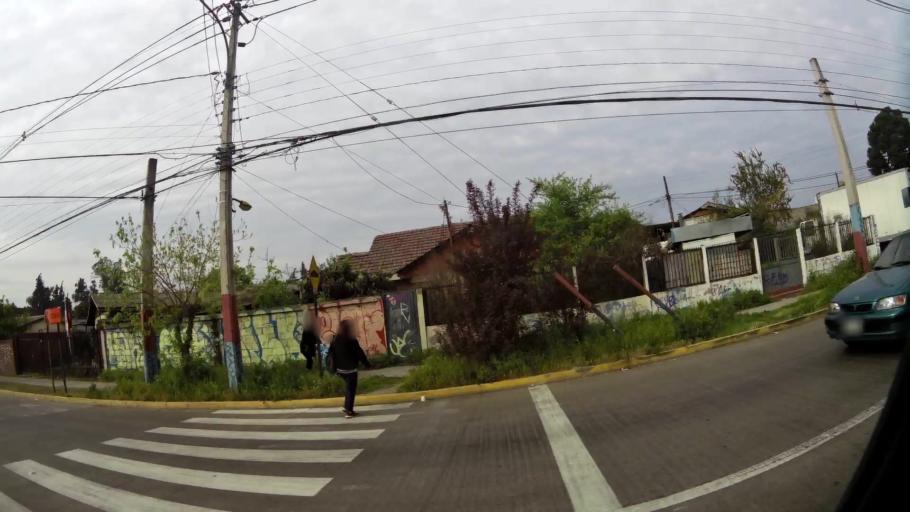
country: CL
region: Santiago Metropolitan
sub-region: Provincia de Santiago
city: Lo Prado
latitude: -33.5141
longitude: -70.7517
